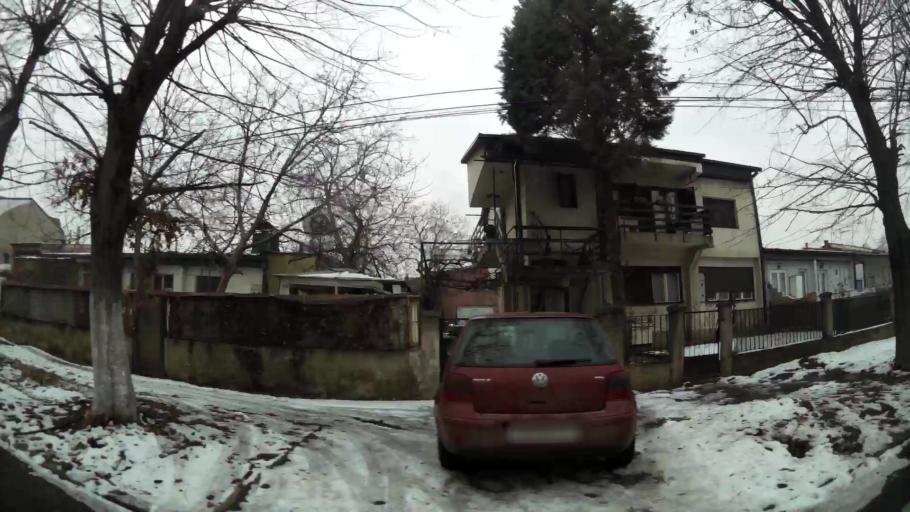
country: MK
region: Cair
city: Cair
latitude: 42.0160
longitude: 21.4599
